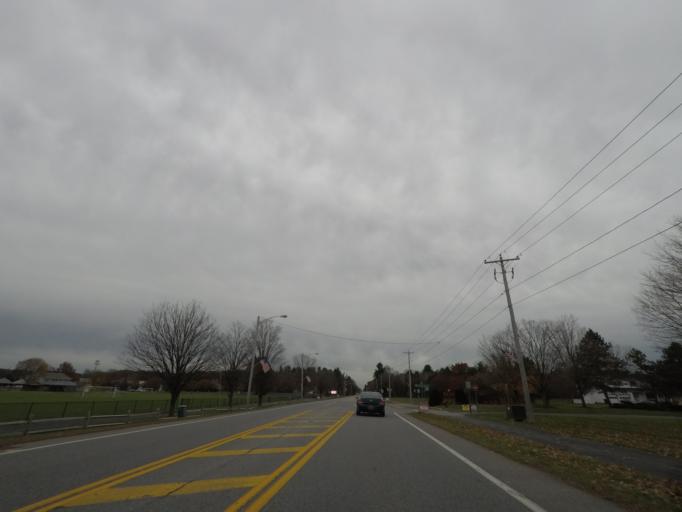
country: US
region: New York
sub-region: Saratoga County
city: Country Knolls
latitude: 42.8649
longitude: -73.8204
